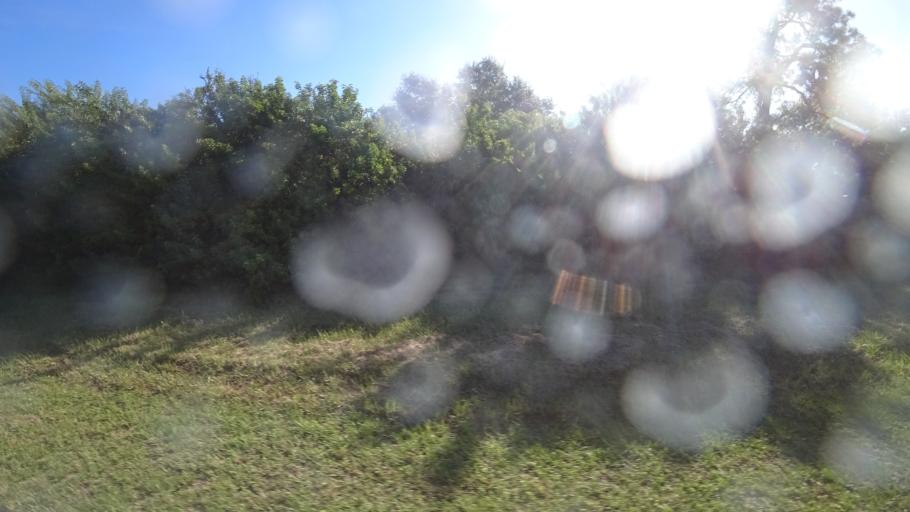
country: US
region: Florida
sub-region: Manatee County
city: Memphis
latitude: 27.6395
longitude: -82.5399
